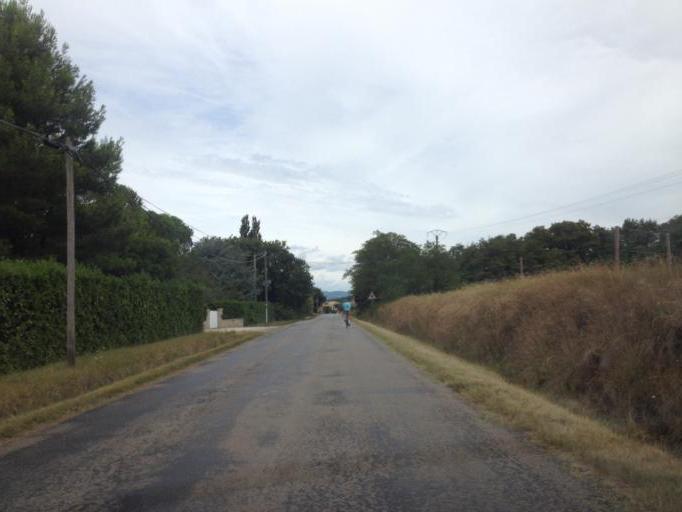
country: FR
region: Rhone-Alpes
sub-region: Departement de la Drome
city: Allan
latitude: 44.4932
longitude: 4.7897
